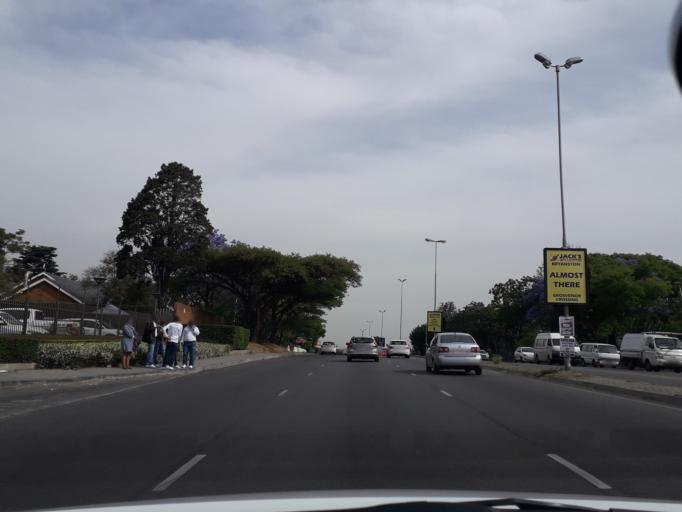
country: ZA
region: Gauteng
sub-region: City of Johannesburg Metropolitan Municipality
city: Diepsloot
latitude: -26.0537
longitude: 28.0217
